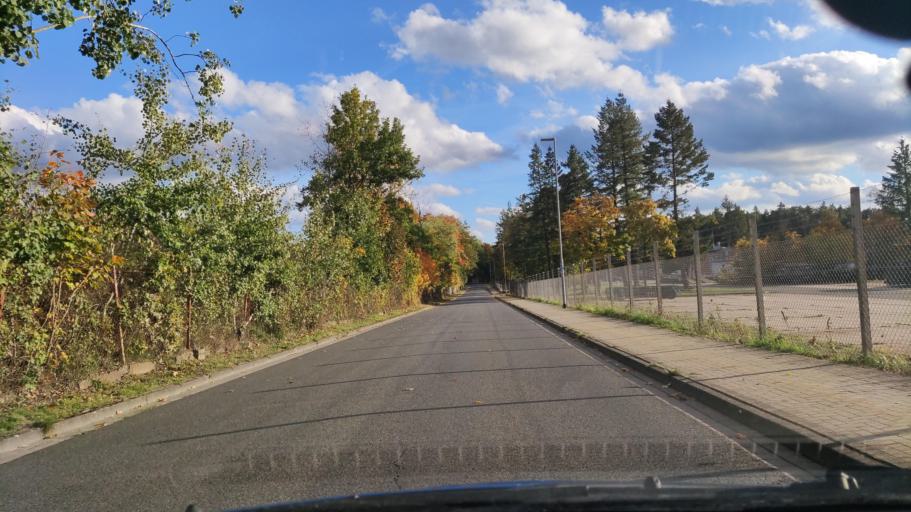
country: DE
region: Lower Saxony
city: Munster
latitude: 52.9773
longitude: 10.0797
